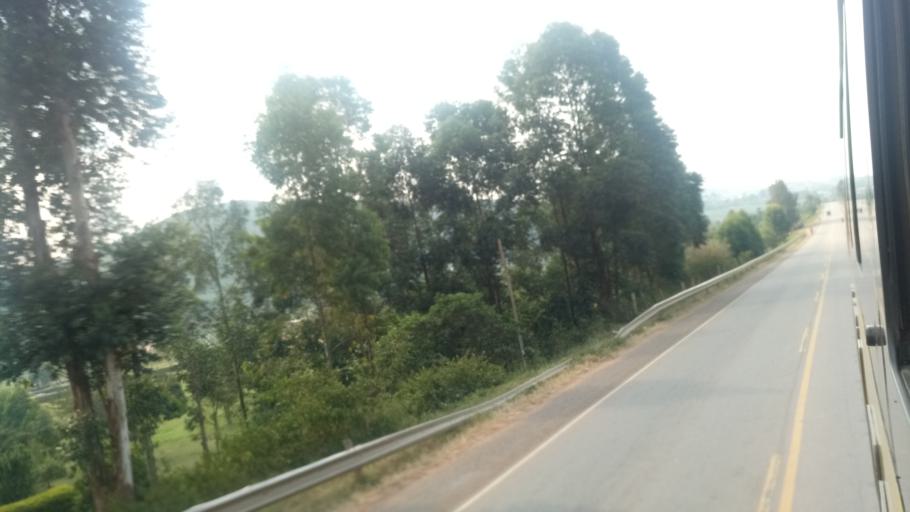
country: UG
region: Western Region
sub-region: Mbarara District
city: Mbarara
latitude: -0.5432
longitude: 30.7138
